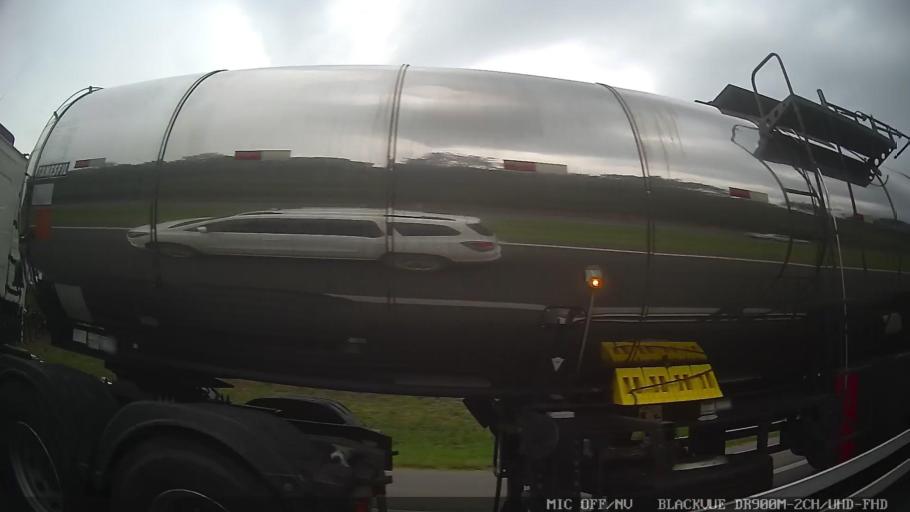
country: BR
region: Sao Paulo
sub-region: Jarinu
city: Jarinu
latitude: -23.0284
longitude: -46.7446
